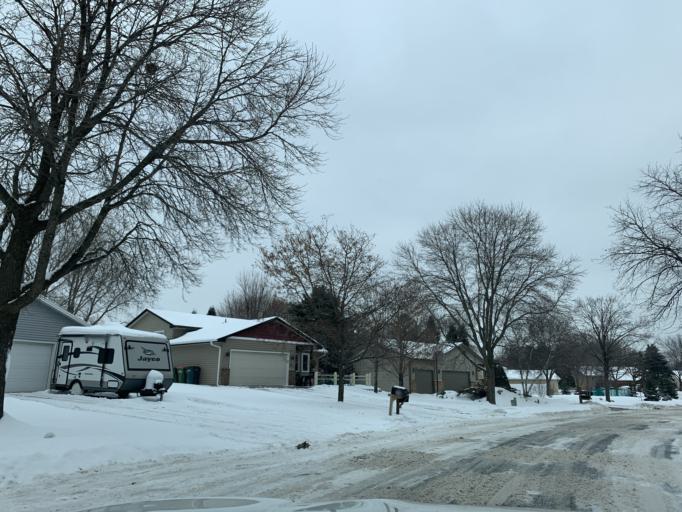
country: US
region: Minnesota
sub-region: Hennepin County
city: West Coon Rapids
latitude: 45.1640
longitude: -93.3033
